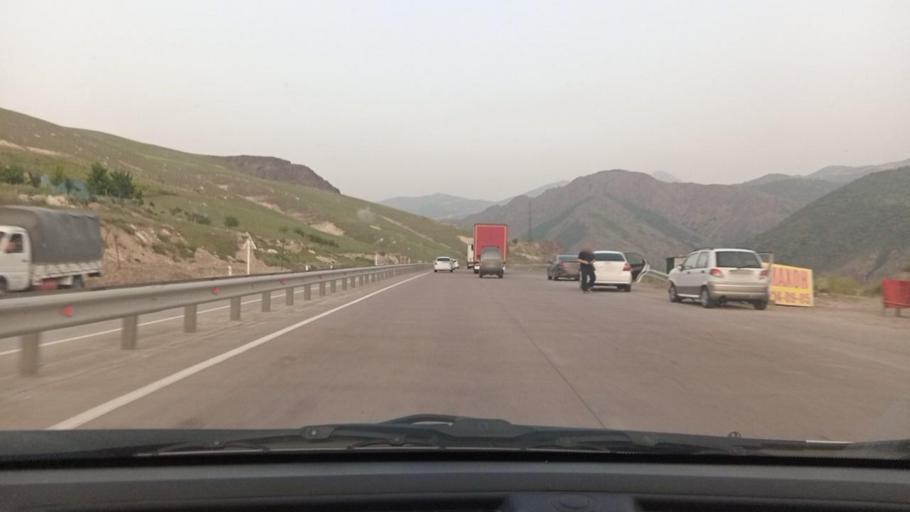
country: UZ
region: Toshkent
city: Angren
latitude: 41.0747
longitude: 70.2638
